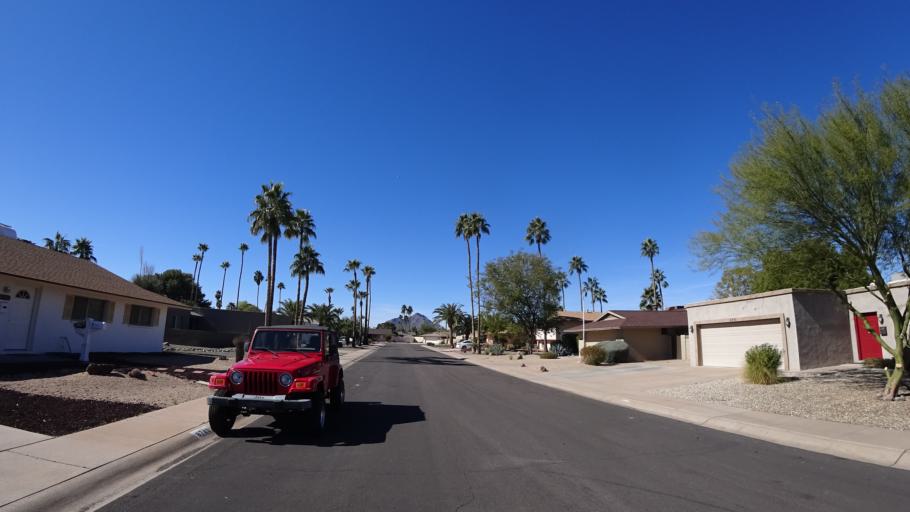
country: US
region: Arizona
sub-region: Maricopa County
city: Scottsdale
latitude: 33.5114
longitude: -111.8919
